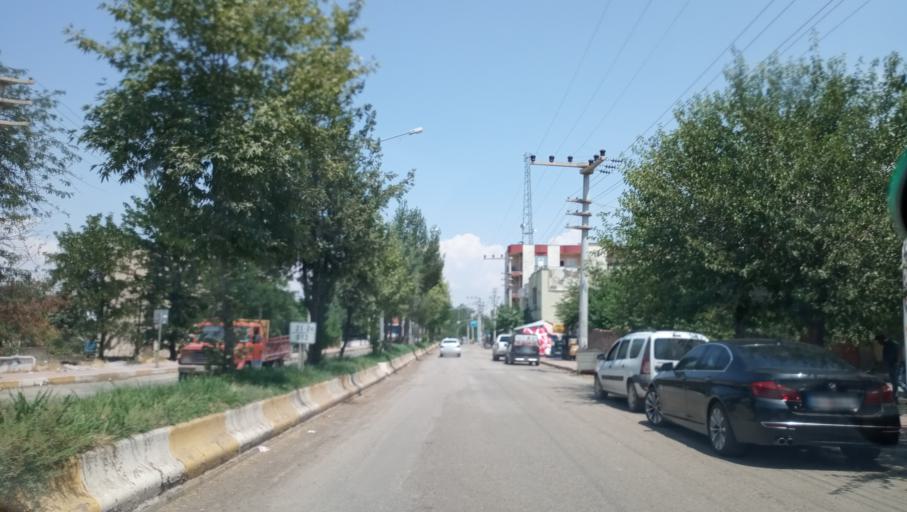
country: TR
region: Diyarbakir
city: Tepe
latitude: 37.7927
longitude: 40.7757
